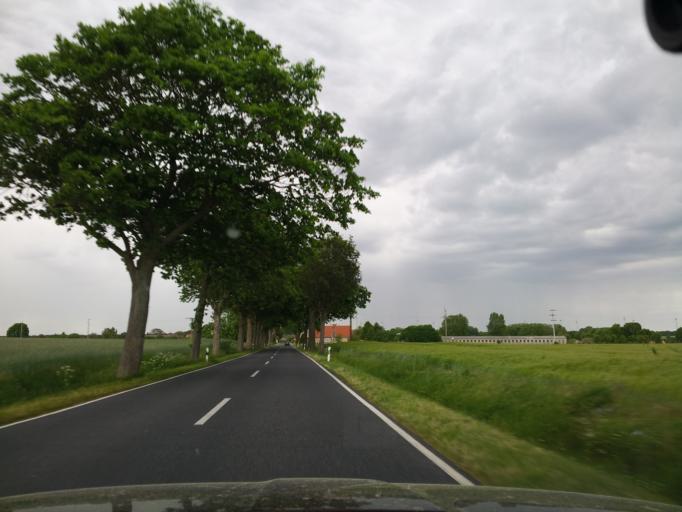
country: DE
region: Brandenburg
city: Niedergorsdorf
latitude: 52.0001
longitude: 12.9341
